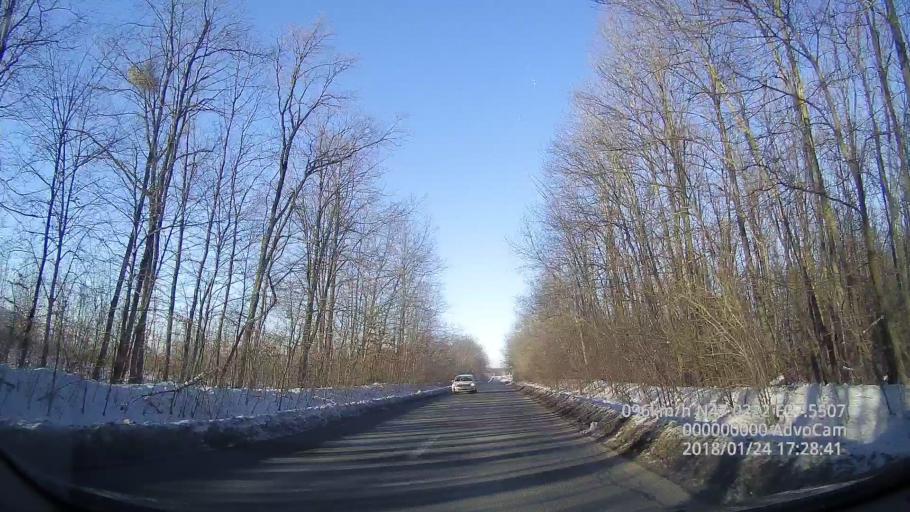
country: RO
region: Iasi
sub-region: Comuna Mogosesti
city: Mogosesti
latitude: 47.0231
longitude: 27.5506
